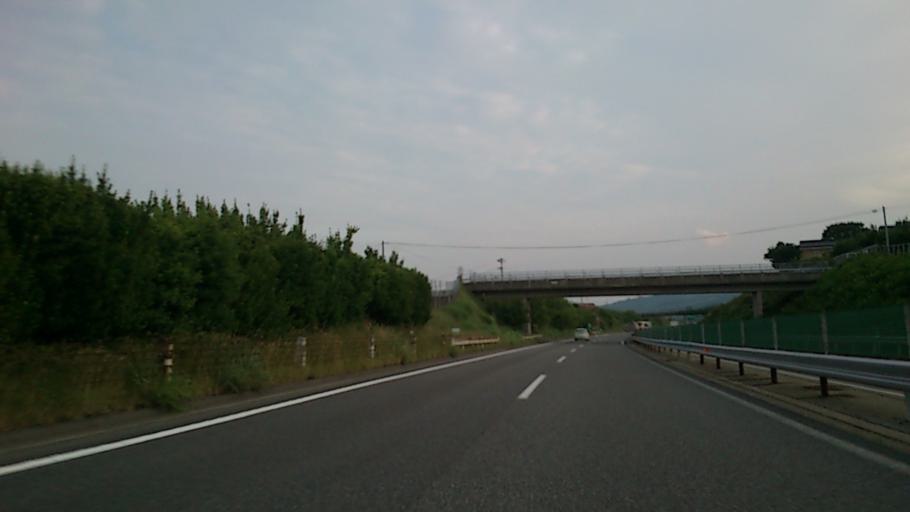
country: JP
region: Nagano
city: Iida
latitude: 35.6313
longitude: 137.8950
